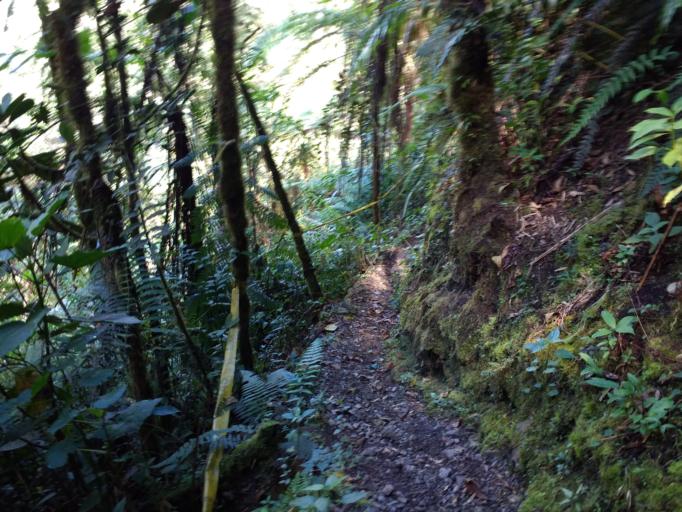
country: PE
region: Cusco
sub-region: Provincia de La Convencion
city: Maranura
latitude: -12.9707
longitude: -72.5312
